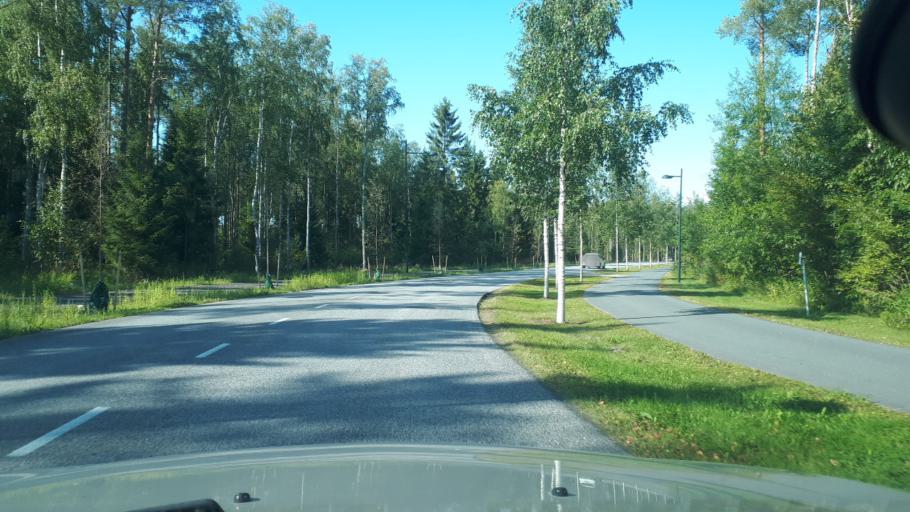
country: FI
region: Northern Ostrobothnia
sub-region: Oulu
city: Oulu
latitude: 65.0639
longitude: 25.4454
